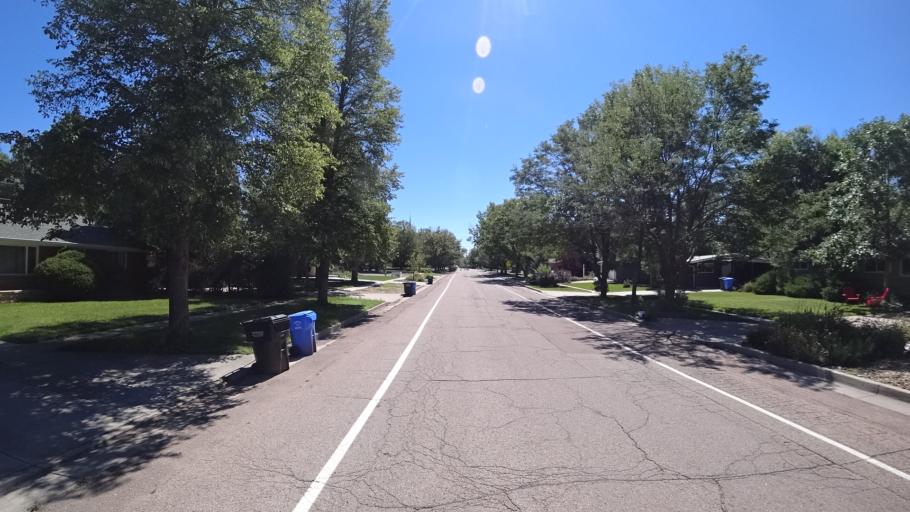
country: US
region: Colorado
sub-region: El Paso County
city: Colorado Springs
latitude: 38.8657
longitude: -104.8057
